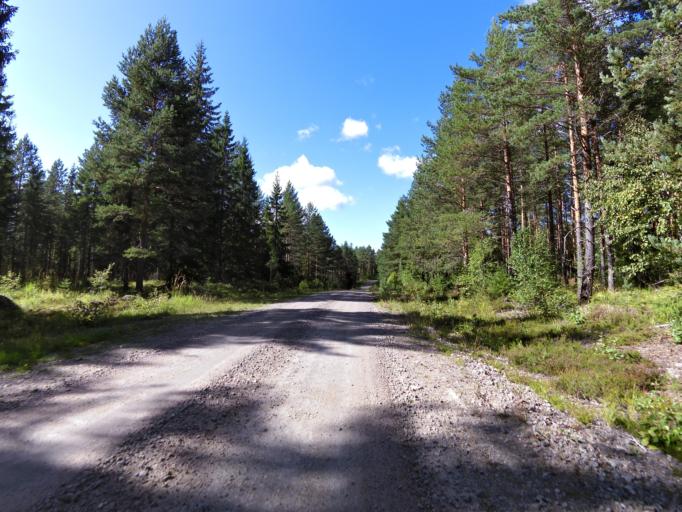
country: SE
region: Gaevleborg
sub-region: Ockelbo Kommun
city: Ockelbo
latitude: 60.7964
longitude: 16.8130
